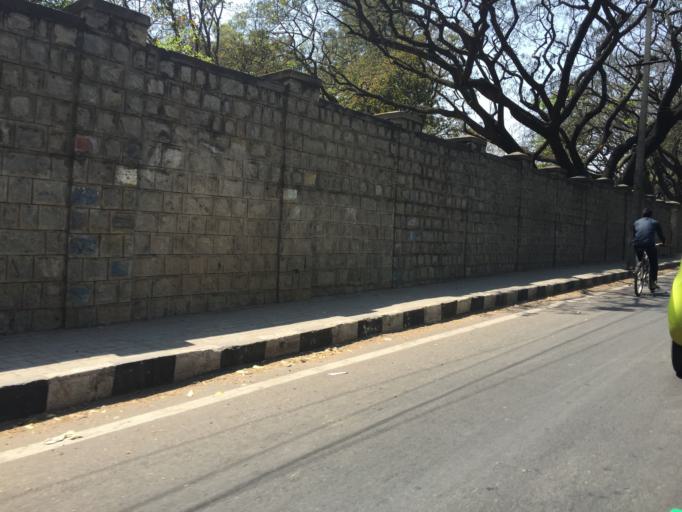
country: IN
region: Karnataka
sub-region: Bangalore Urban
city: Bangalore
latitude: 12.9822
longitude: 77.6330
